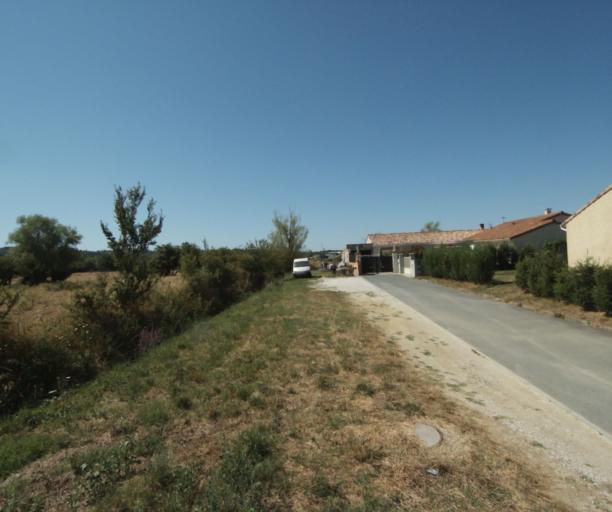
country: FR
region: Midi-Pyrenees
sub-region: Departement de la Haute-Garonne
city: Revel
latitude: 43.4615
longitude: 1.9893
